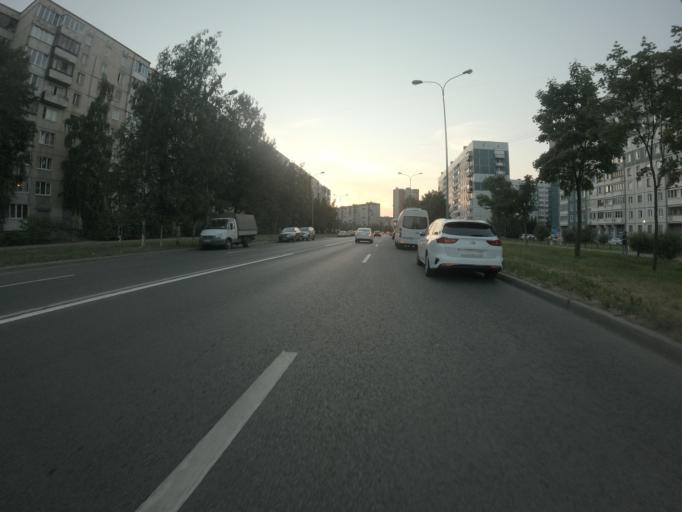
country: RU
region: St.-Petersburg
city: Krasnogvargeisky
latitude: 59.9147
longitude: 30.4585
